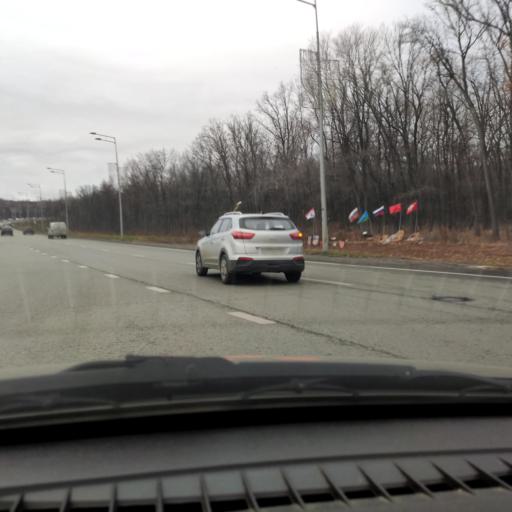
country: RU
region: Samara
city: Petra-Dubrava
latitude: 53.3089
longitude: 50.2355
